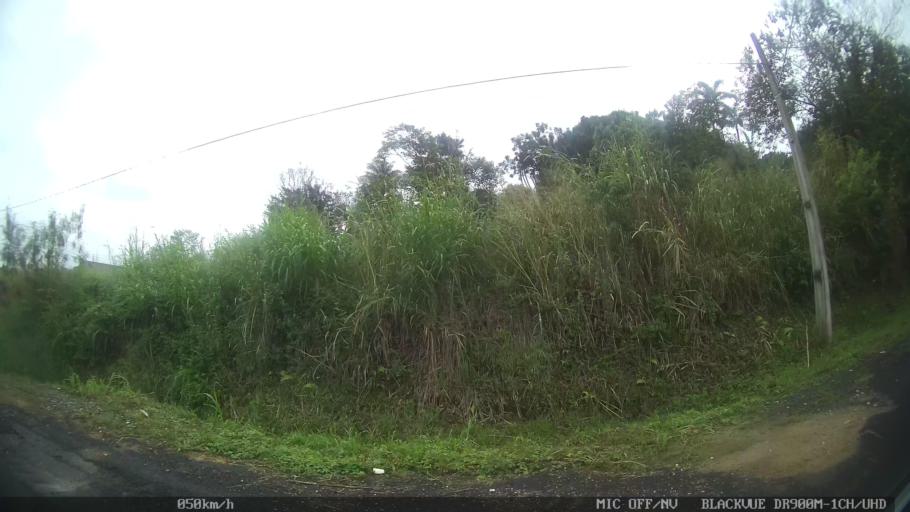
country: BR
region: Sao Paulo
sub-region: Cajati
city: Cajati
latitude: -24.7239
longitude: -48.1023
